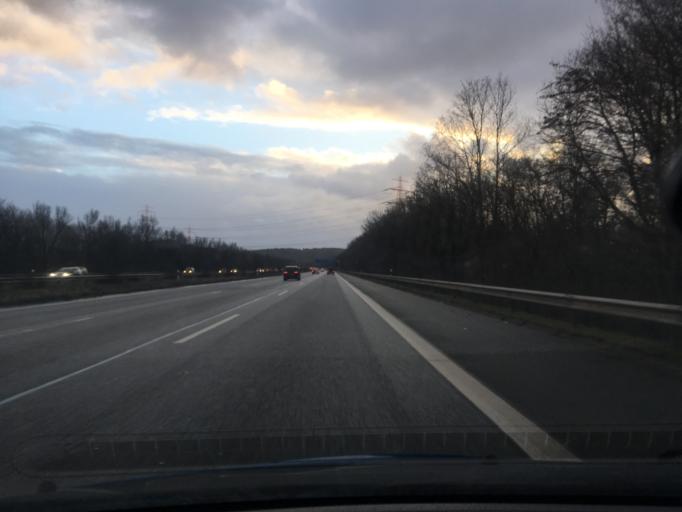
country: DE
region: Hamburg
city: Altona
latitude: 53.4905
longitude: 9.9136
